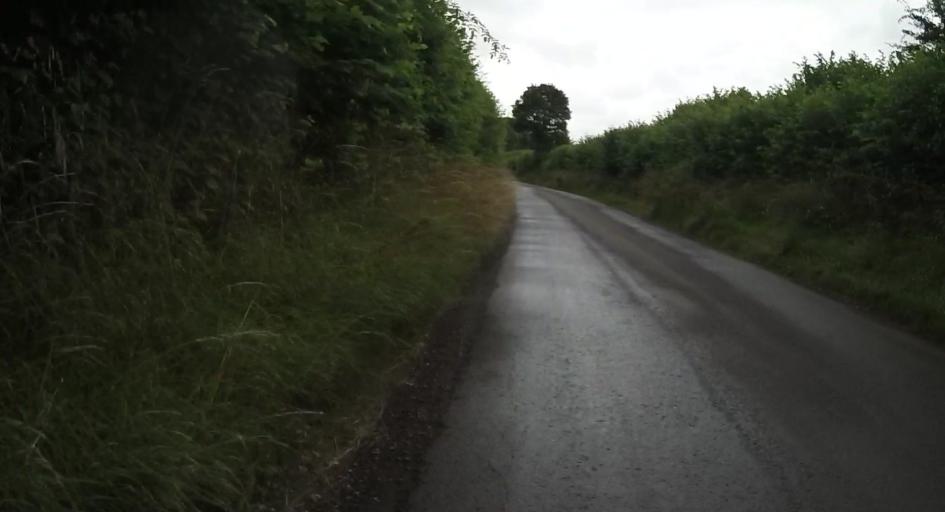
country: GB
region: England
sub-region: Hampshire
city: Andover
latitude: 51.2057
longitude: -1.4277
